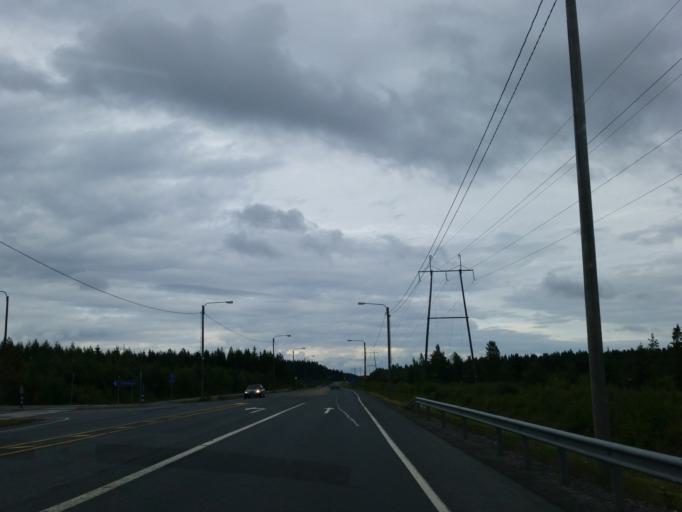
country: FI
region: Northern Savo
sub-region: Kuopio
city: Kuopio
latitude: 62.9833
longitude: 27.7359
